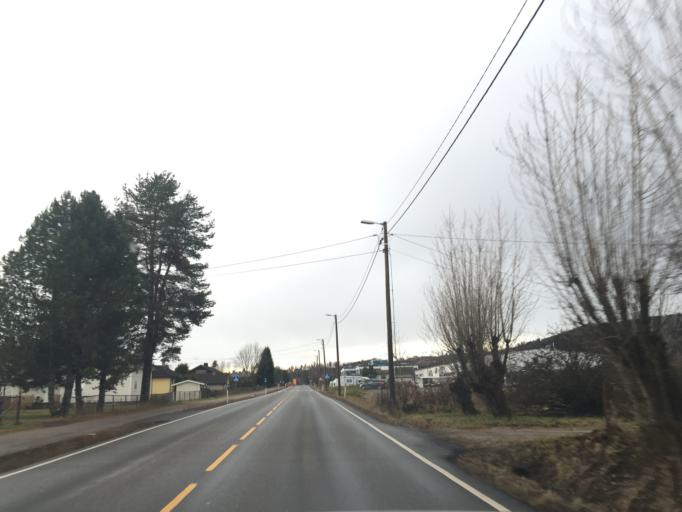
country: NO
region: Hedmark
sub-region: Asnes
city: Flisa
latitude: 60.6132
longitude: 12.0275
